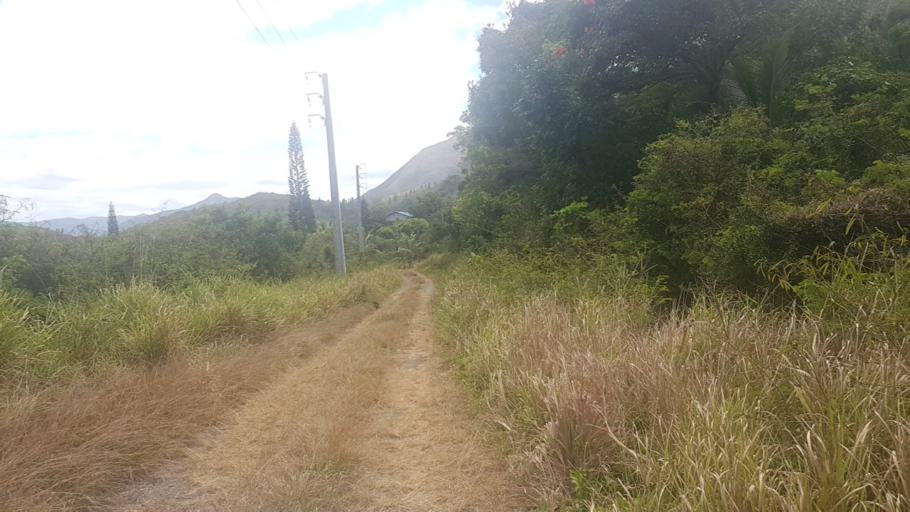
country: NC
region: South Province
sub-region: Dumbea
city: Dumbea
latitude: -22.1850
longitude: 166.4792
